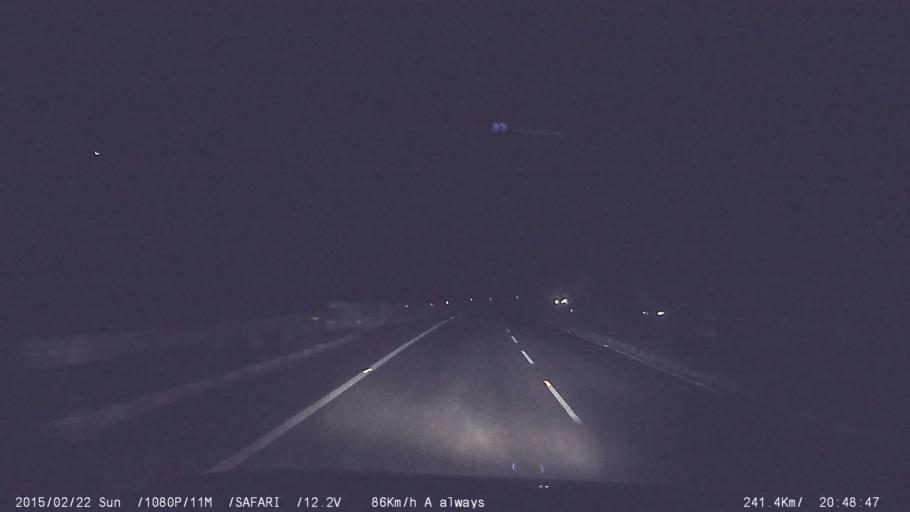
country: IN
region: Tamil Nadu
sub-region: Dindigul
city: Vedasandur
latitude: 10.5100
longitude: 77.9380
